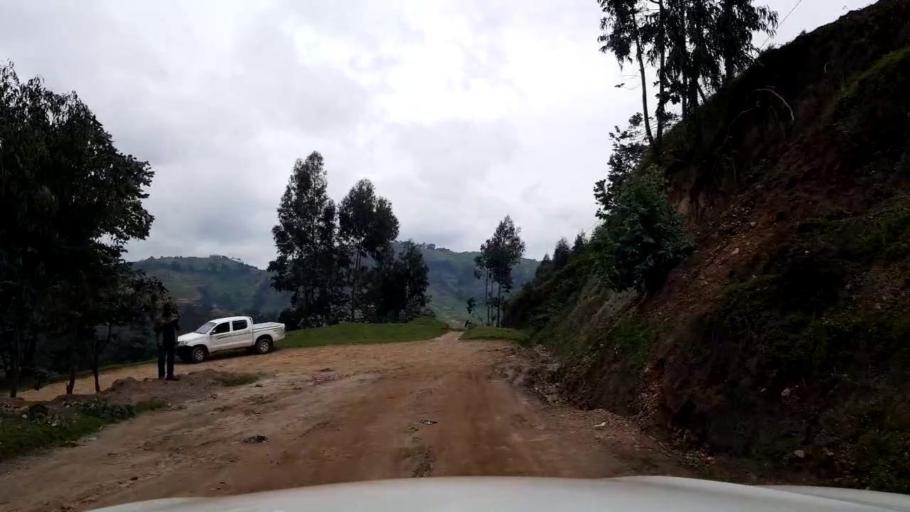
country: RW
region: Western Province
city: Kibuye
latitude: -1.9576
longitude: 29.4239
